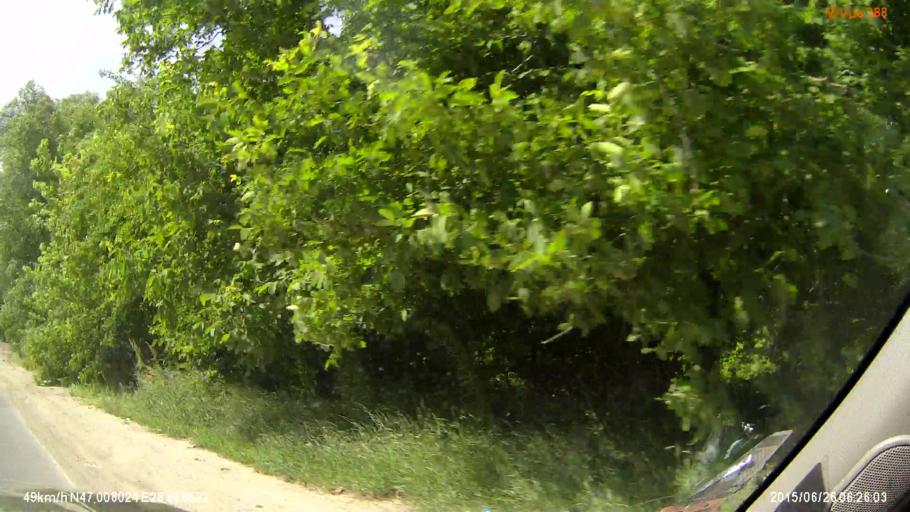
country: MD
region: Chisinau
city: Chisinau
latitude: 47.0081
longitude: 28.8764
